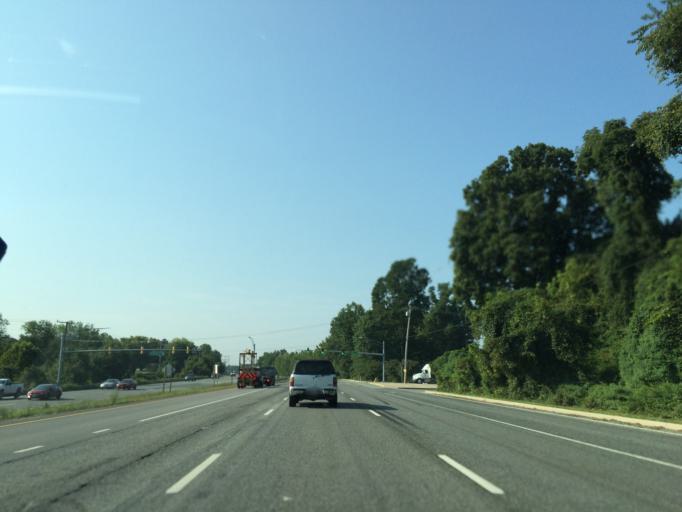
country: US
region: Maryland
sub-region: Prince George's County
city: Marlboro Meadows
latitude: 38.8607
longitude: -76.7248
